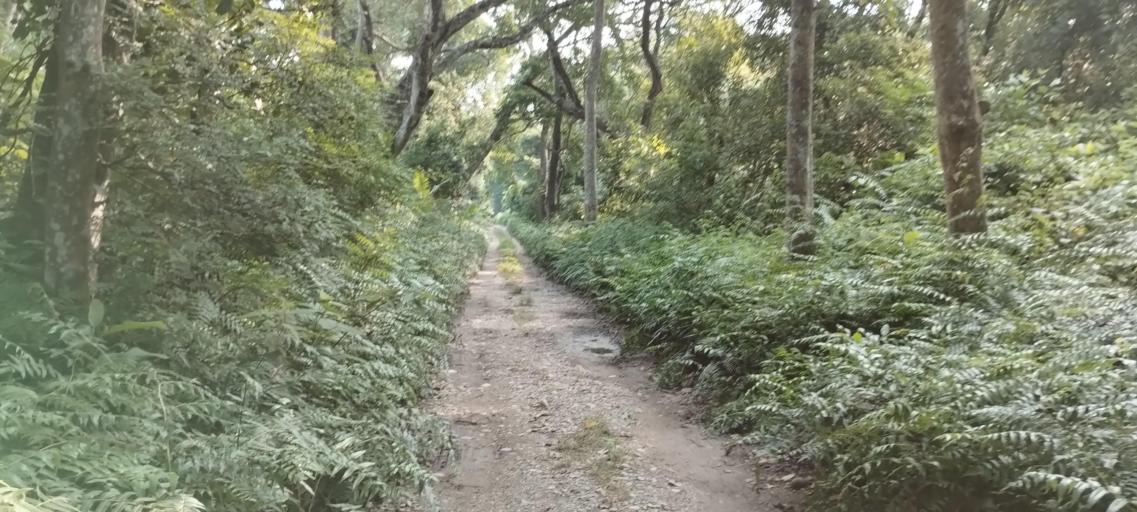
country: NP
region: Far Western
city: Tikapur
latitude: 28.4637
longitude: 81.2437
